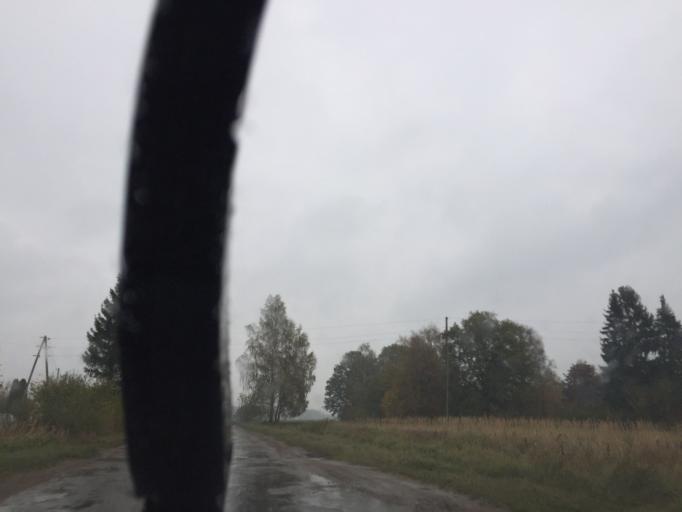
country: LV
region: Dobeles Rajons
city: Dobele
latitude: 56.6879
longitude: 23.4424
